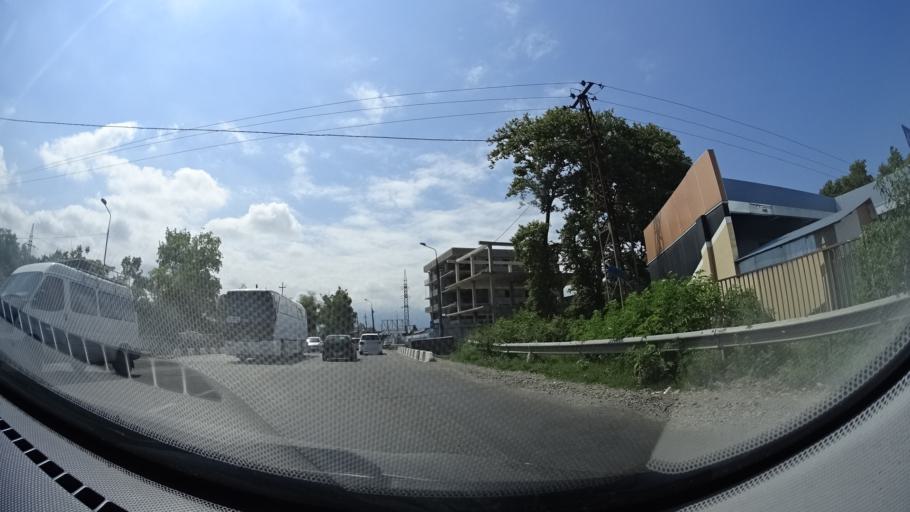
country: GE
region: Ajaria
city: Batumi
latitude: 41.6206
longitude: 41.6167
